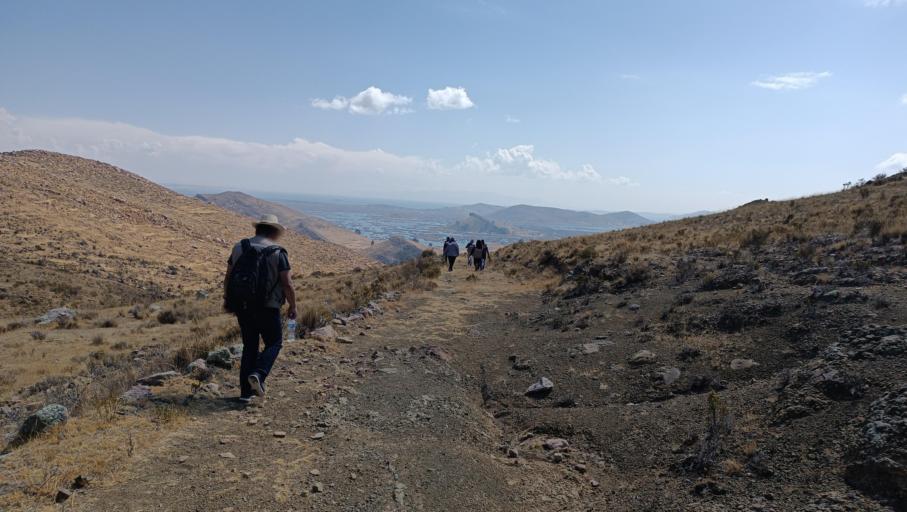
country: BO
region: La Paz
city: Batallas
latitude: -16.3505
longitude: -68.6524
